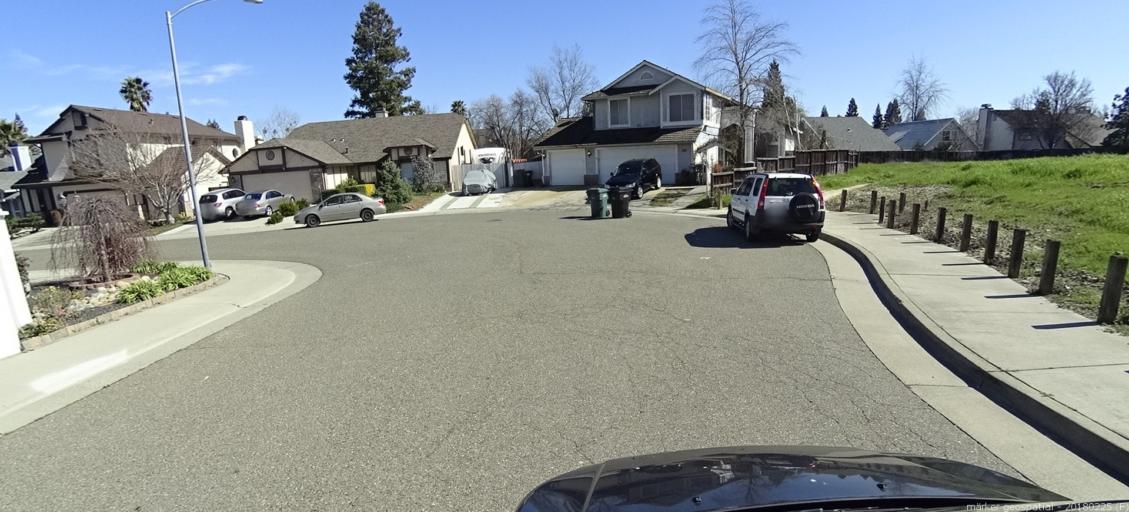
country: US
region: California
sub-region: Sacramento County
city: Antelope
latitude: 38.7172
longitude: -121.3559
